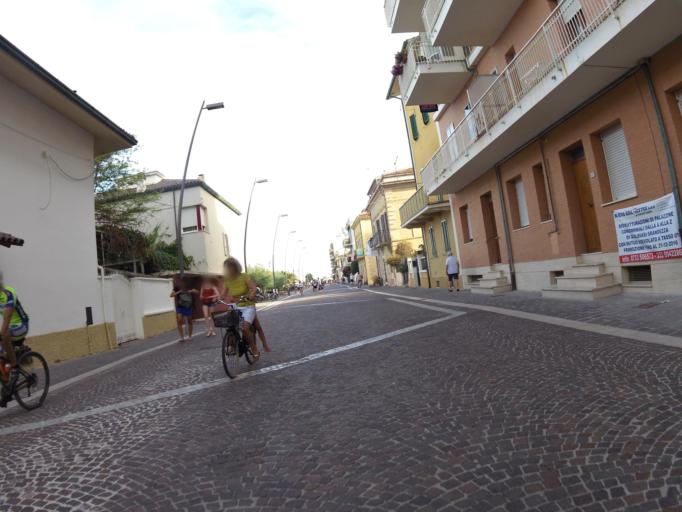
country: IT
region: The Marches
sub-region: Provincia di Macerata
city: Porto Recanati
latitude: 43.4302
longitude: 13.6670
